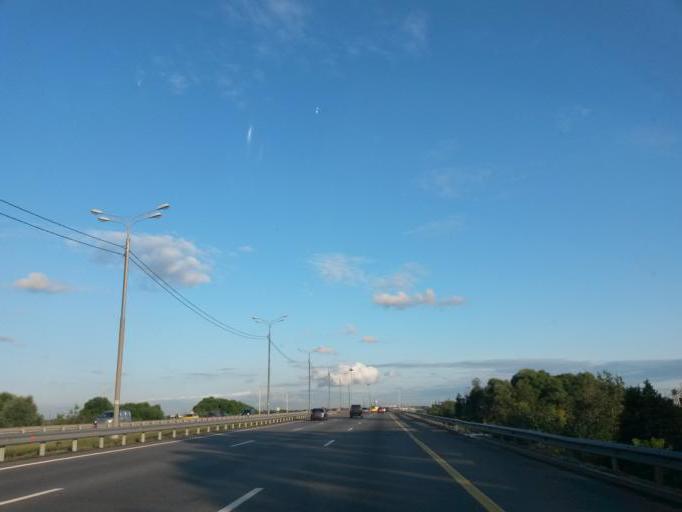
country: RU
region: Moskovskaya
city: Yam
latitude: 55.4986
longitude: 37.7288
